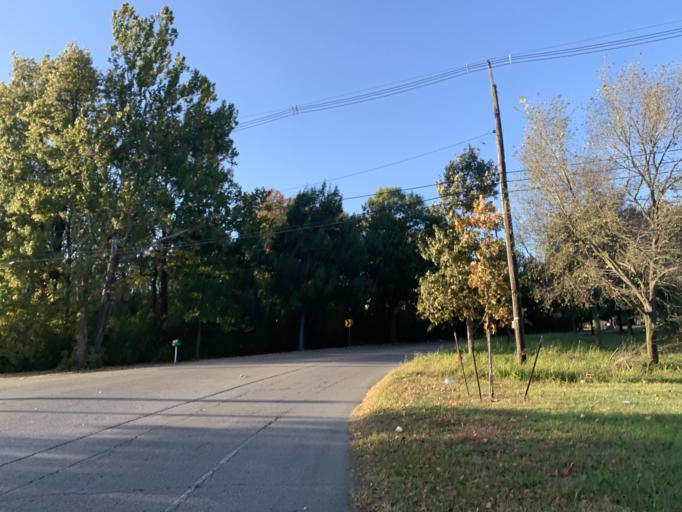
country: US
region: Kentucky
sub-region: Jefferson County
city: Shively
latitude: 38.2328
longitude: -85.8306
